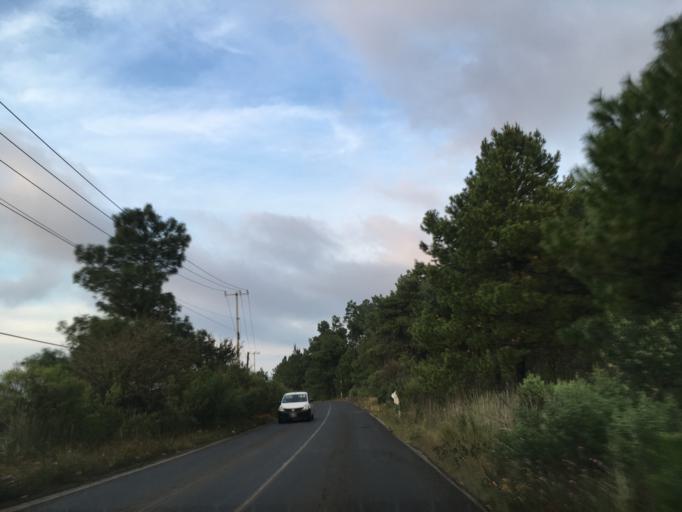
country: MX
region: Michoacan
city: Angahuan
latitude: 19.5725
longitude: -102.2361
